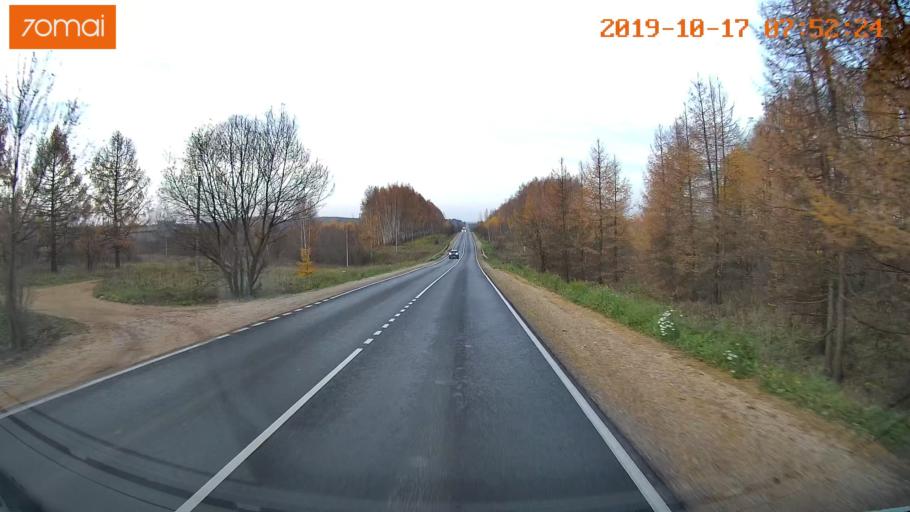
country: RU
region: Vladimir
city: Yur'yev-Pol'skiy
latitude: 56.4730
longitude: 39.6412
